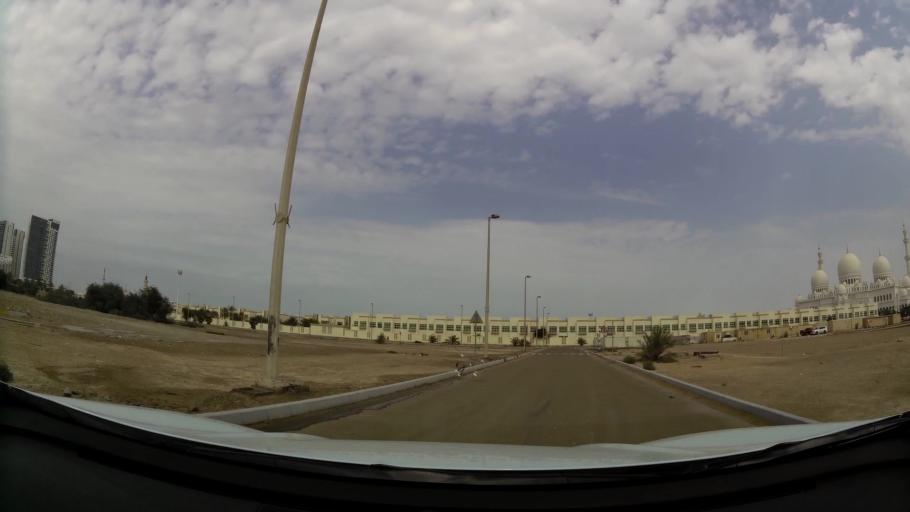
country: AE
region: Abu Dhabi
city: Abu Dhabi
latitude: 24.4095
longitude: 54.4698
